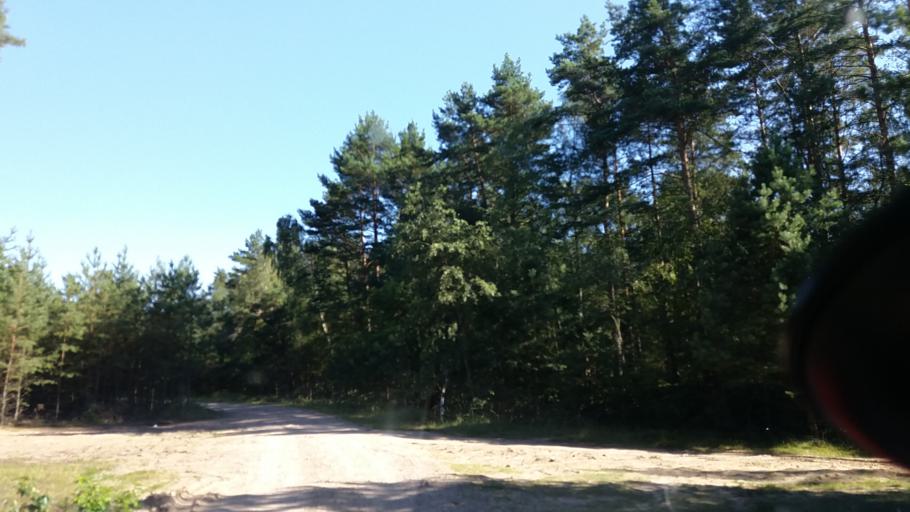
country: PL
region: West Pomeranian Voivodeship
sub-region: Powiat szczecinecki
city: Borne Sulinowo
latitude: 53.5562
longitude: 16.5064
